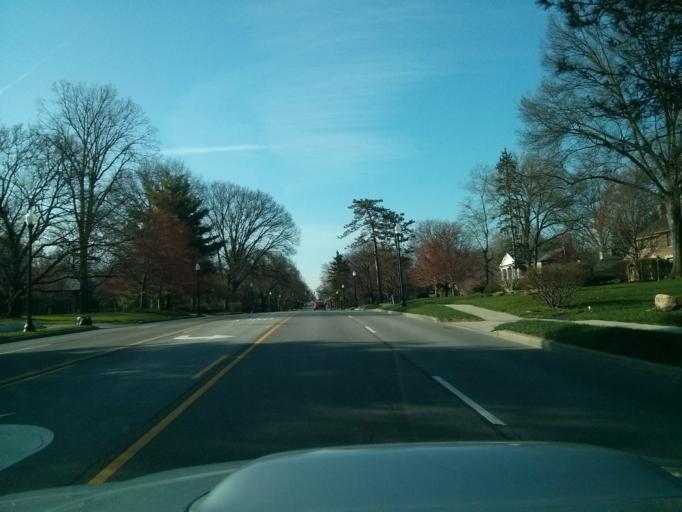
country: US
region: Indiana
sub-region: Marion County
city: Broad Ripple
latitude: 39.8562
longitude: -86.1572
